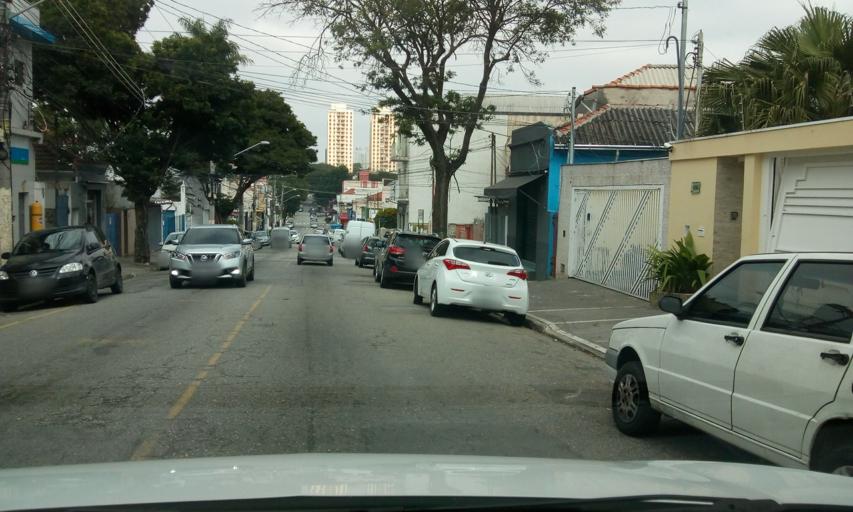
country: BR
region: Sao Paulo
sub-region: Sao Paulo
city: Sao Paulo
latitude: -23.5548
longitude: -46.5842
